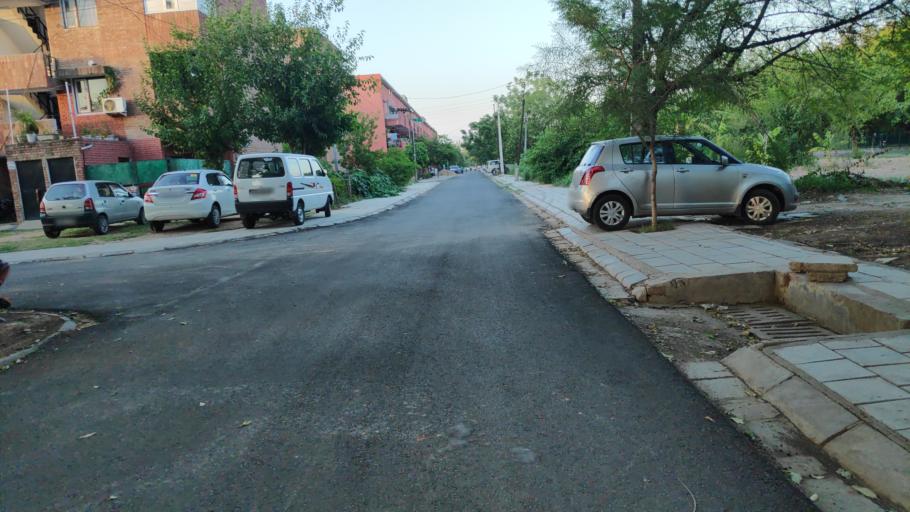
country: IN
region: Punjab
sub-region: Ajitgarh
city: Mohali
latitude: 30.7206
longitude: 76.7424
